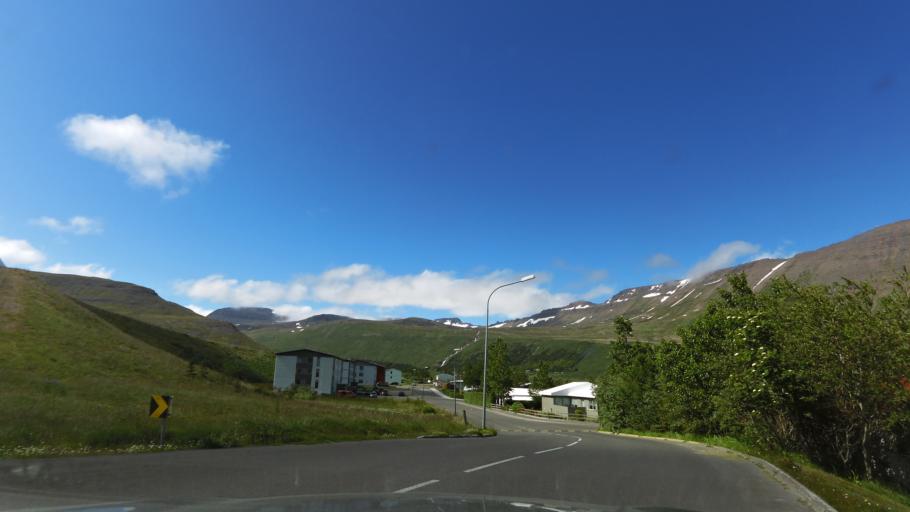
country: IS
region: Westfjords
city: Isafjoerdur
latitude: 66.0543
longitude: -23.1731
